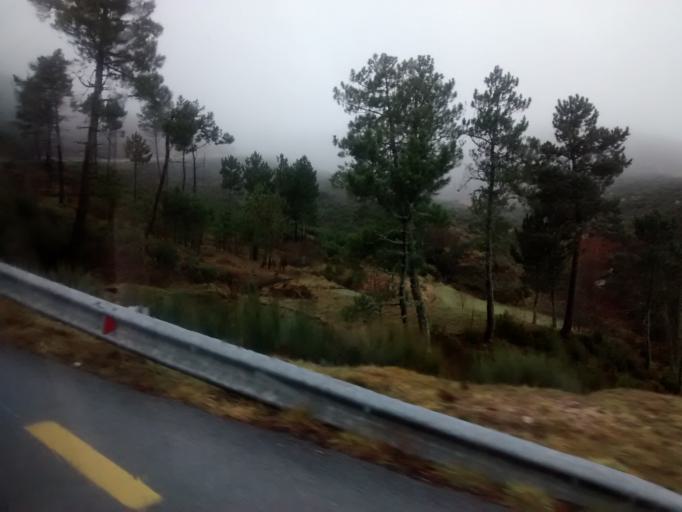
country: PT
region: Guarda
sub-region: Seia
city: Seia
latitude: 40.3974
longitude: -7.6502
